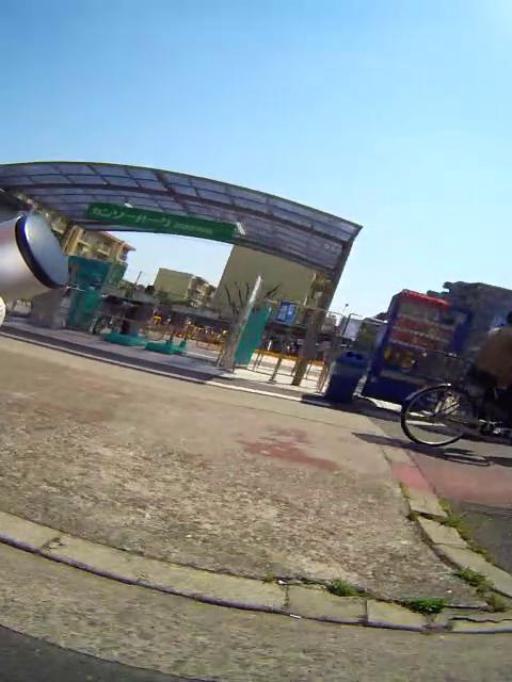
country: JP
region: Osaka
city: Matsubara
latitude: 34.6100
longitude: 135.5493
